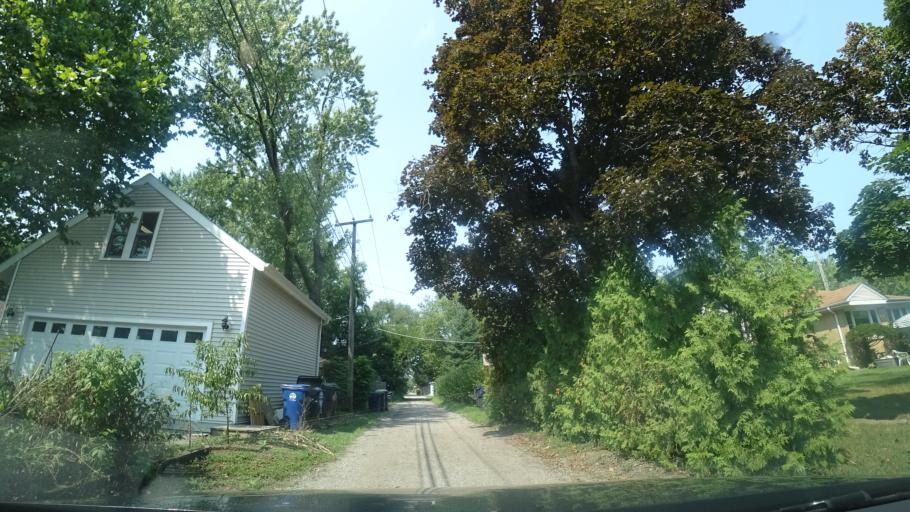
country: US
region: Illinois
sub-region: Cook County
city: Evanston
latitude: 42.0219
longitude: -87.6949
